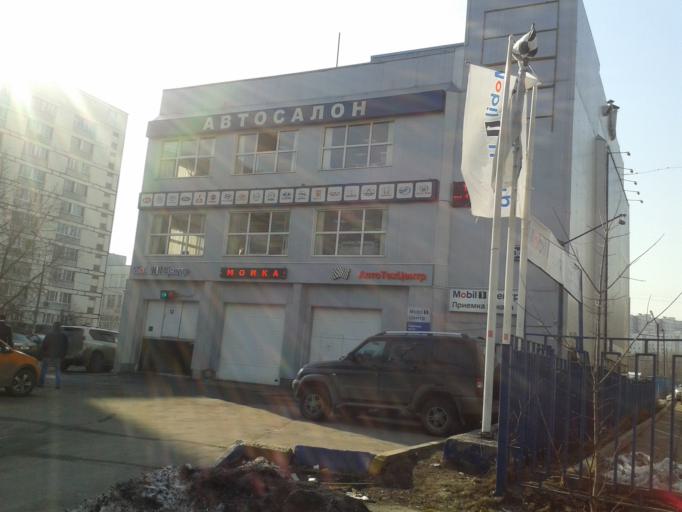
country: RU
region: Moscow
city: Bibirevo
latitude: 55.8891
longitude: 37.5959
